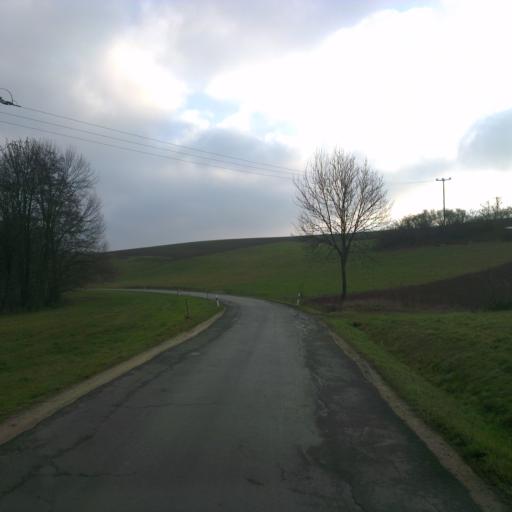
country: DE
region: Thuringia
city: Altenberga
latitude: 50.8334
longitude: 11.5516
